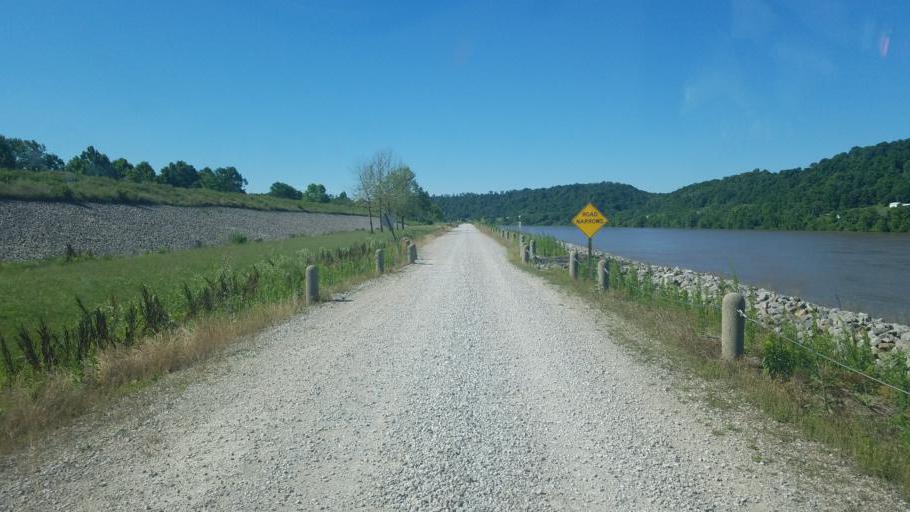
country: US
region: Ohio
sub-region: Gallia County
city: Gallipolis
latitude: 38.6753
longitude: -82.1834
